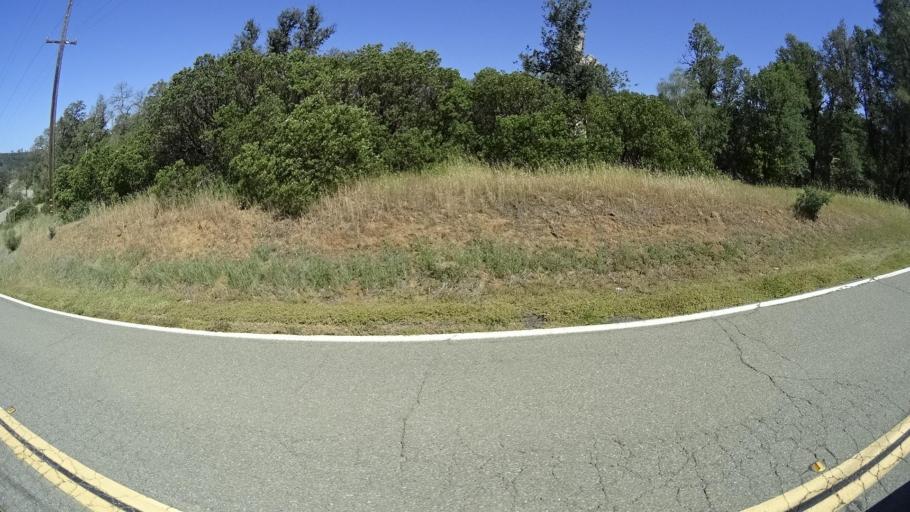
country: US
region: California
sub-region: Lake County
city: Hidden Valley Lake
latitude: 38.8853
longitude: -122.4632
